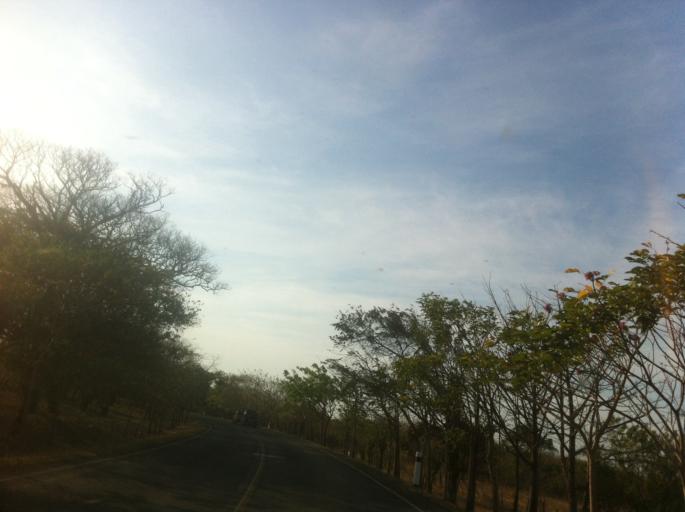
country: NI
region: Rivas
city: Cardenas
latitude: 11.2699
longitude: -85.6495
